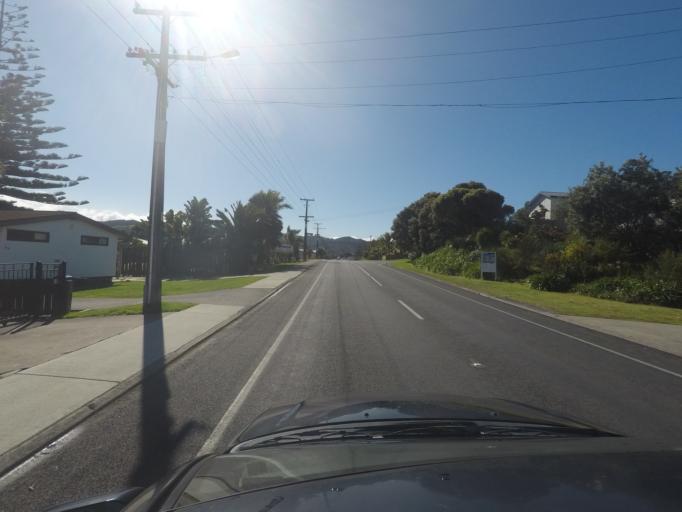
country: NZ
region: Bay of Plenty
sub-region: Western Bay of Plenty District
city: Waihi Beach
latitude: -37.4157
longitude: 175.9479
